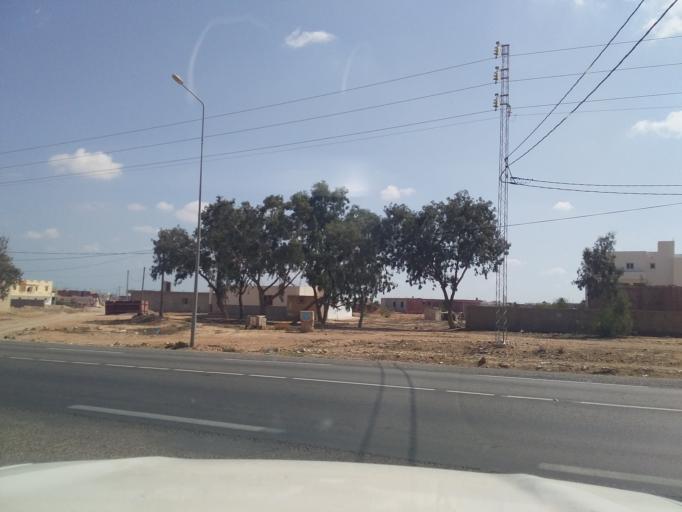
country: TN
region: Madanin
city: Medenine
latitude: 33.5809
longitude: 10.3175
